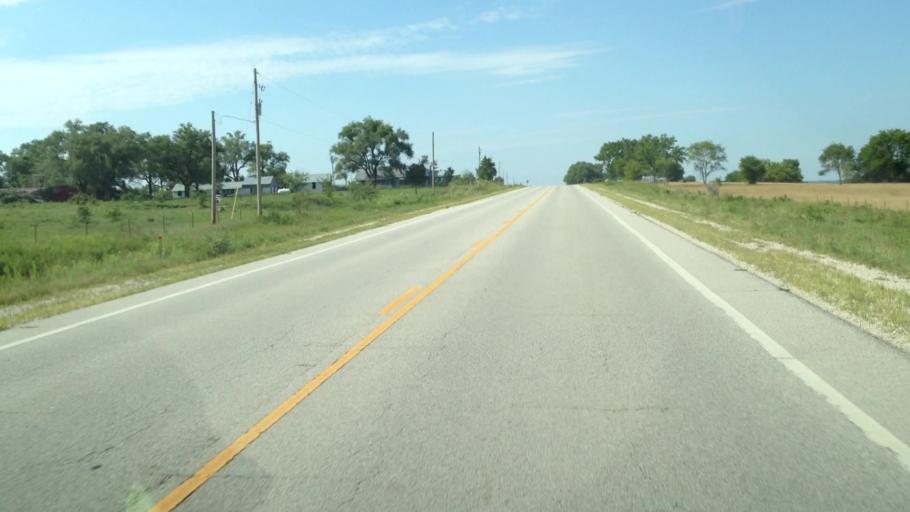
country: US
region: Kansas
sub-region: Neosho County
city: Erie
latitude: 37.4732
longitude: -95.2692
